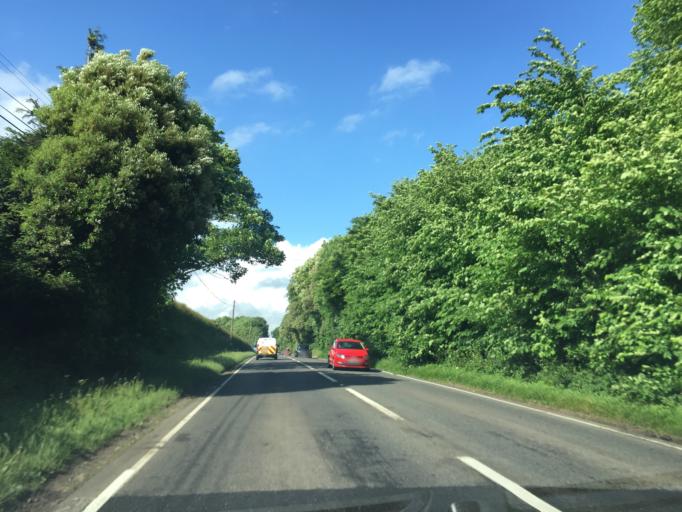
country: GB
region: England
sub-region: Dorset
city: Dorchester
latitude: 50.7238
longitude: -2.4103
